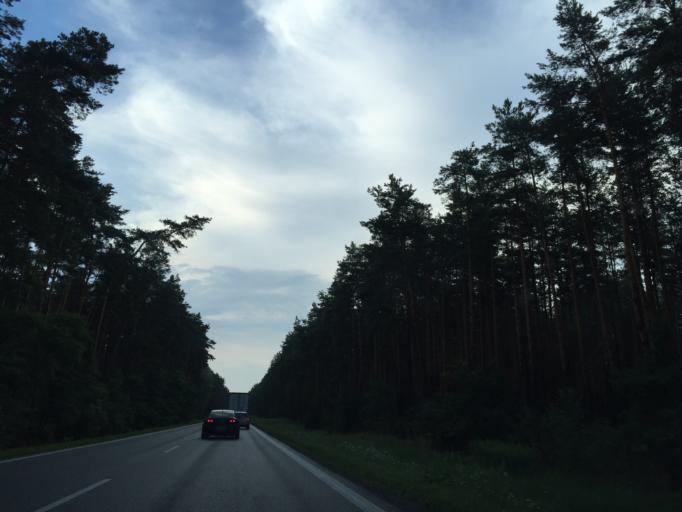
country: PL
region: Masovian Voivodeship
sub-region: Powiat ostrowski
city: Brok
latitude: 52.7145
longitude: 21.8487
